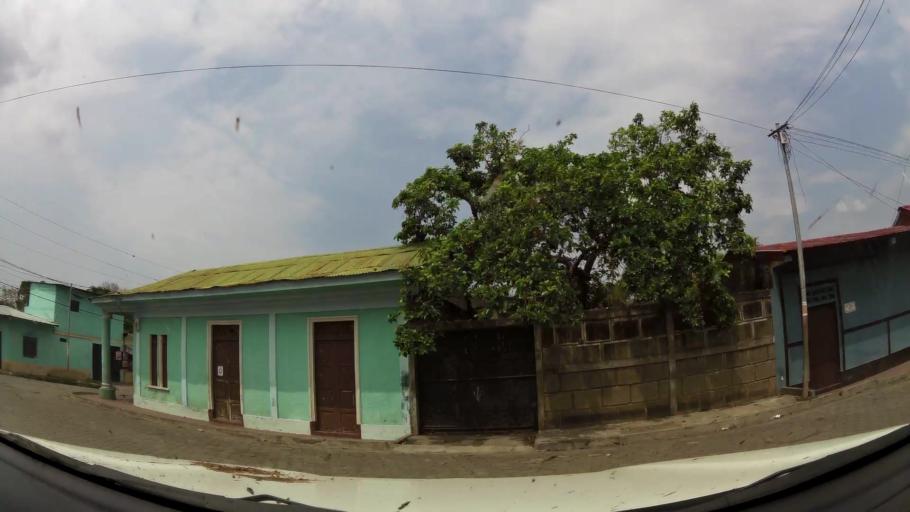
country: NI
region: Granada
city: Diriomo
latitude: 11.8742
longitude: -86.0501
